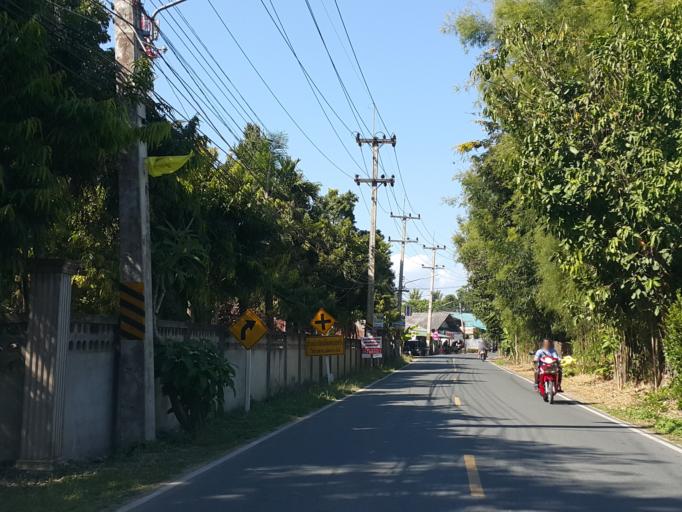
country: TH
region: Chiang Mai
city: Mae Taeng
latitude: 18.9570
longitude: 98.9220
